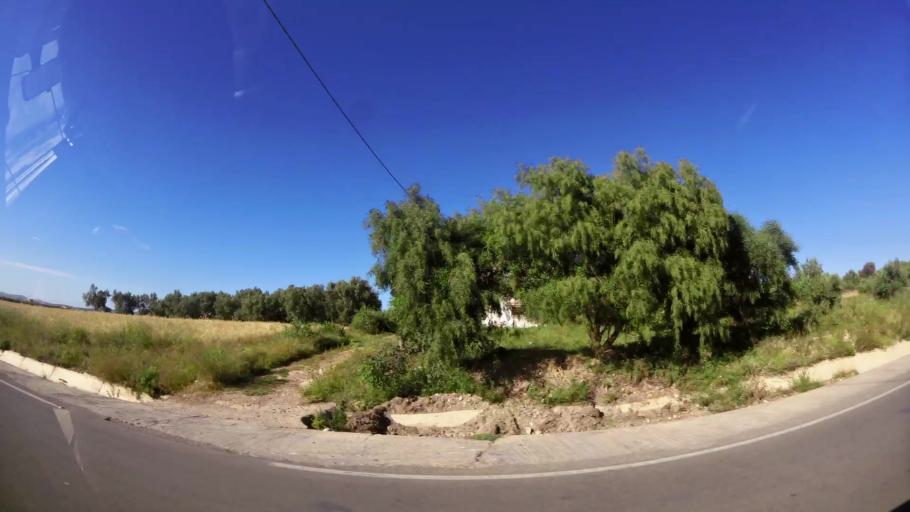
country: MA
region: Oriental
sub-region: Berkane-Taourirt
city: Ahfir
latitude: 34.9644
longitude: -2.1144
